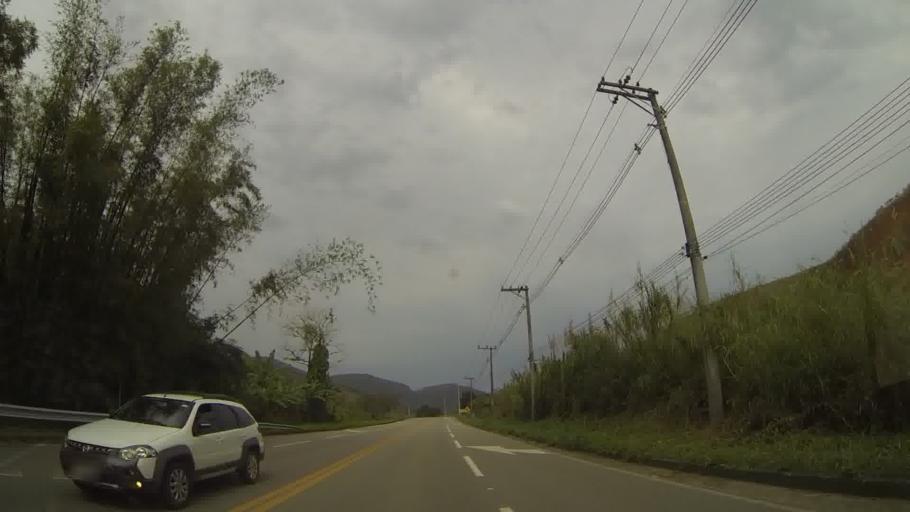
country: BR
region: Sao Paulo
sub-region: Sao Sebastiao
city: Sao Sebastiao
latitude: -23.8048
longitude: -45.5441
